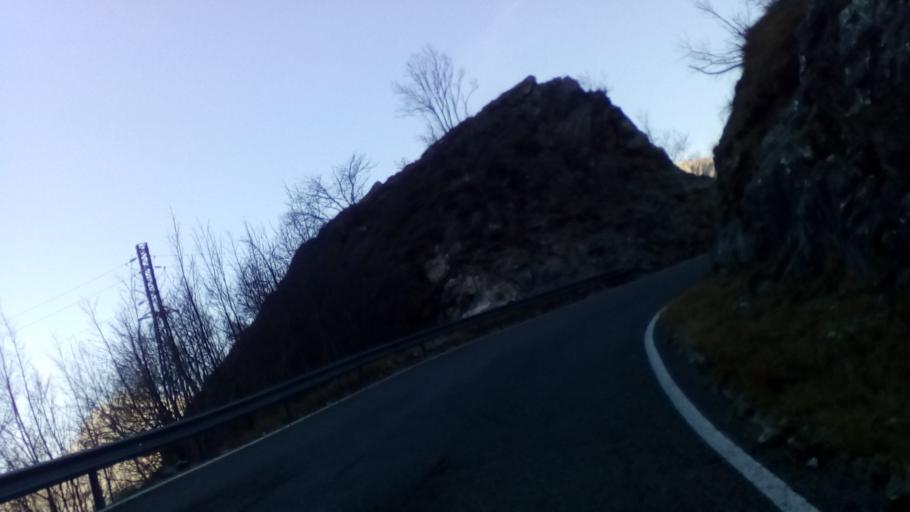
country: IT
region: Tuscany
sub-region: Provincia di Massa-Carrara
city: Montignoso
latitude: 44.0631
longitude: 10.2220
